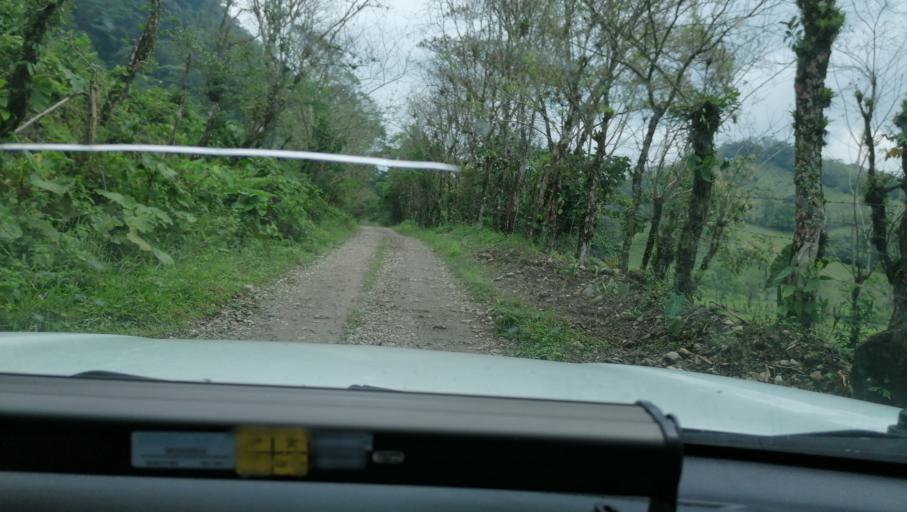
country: MX
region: Chiapas
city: Ixtacomitan
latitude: 17.3520
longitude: -93.1516
